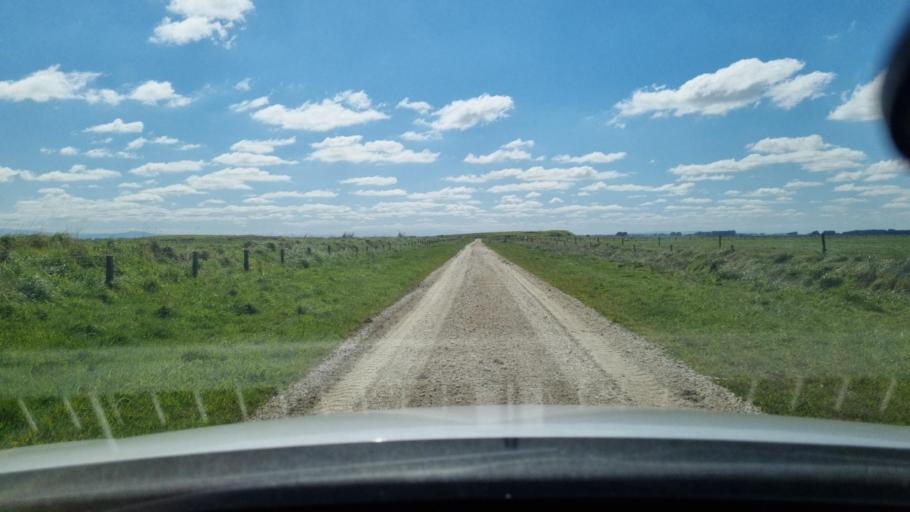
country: NZ
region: Southland
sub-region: Invercargill City
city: Invercargill
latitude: -46.3892
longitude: 168.2592
